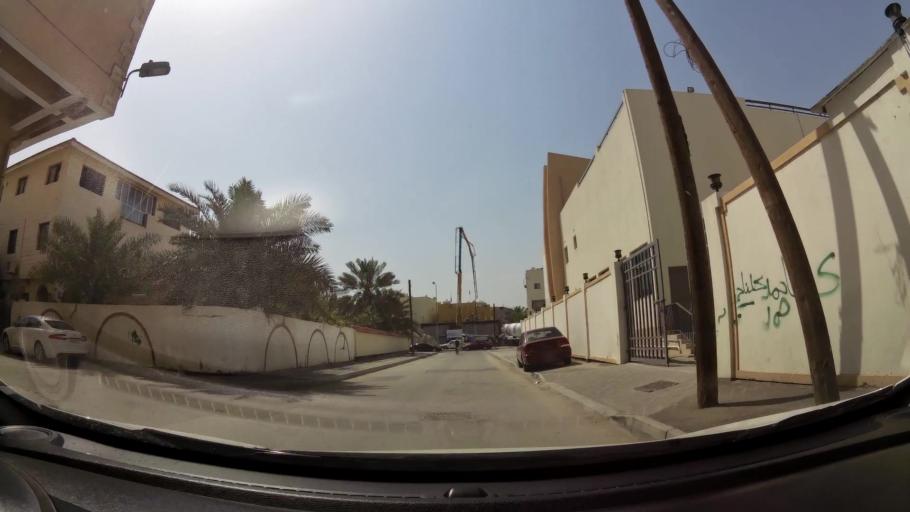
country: BH
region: Manama
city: Jidd Hafs
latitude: 26.2104
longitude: 50.4512
